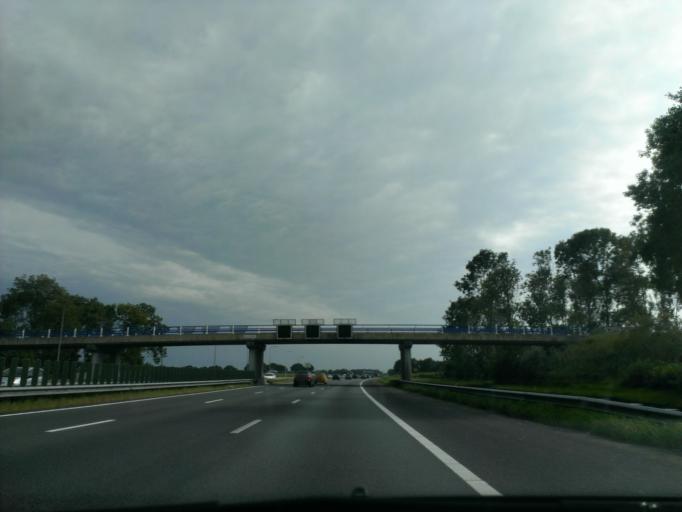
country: NL
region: Overijssel
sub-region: Gemeente Staphorst
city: Staphorst
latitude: 52.6223
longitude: 6.2072
